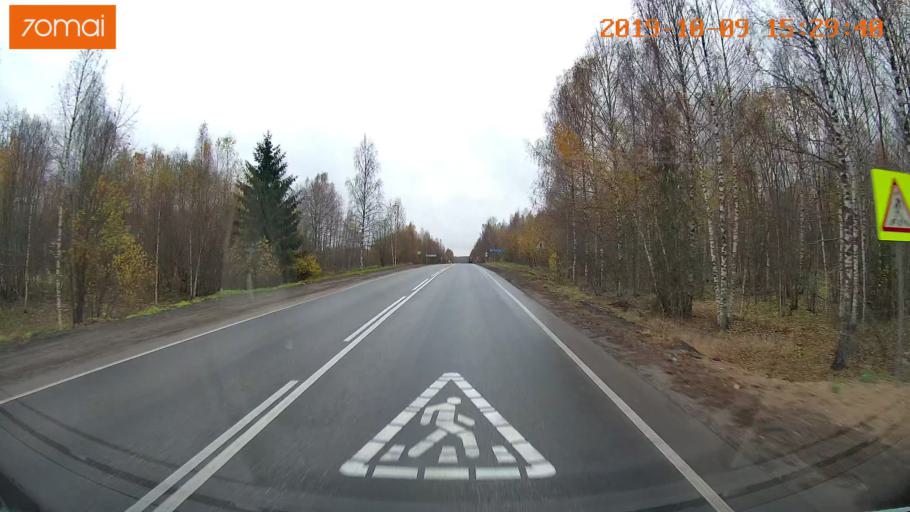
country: RU
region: Kostroma
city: Susanino
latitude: 57.9887
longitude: 41.3387
